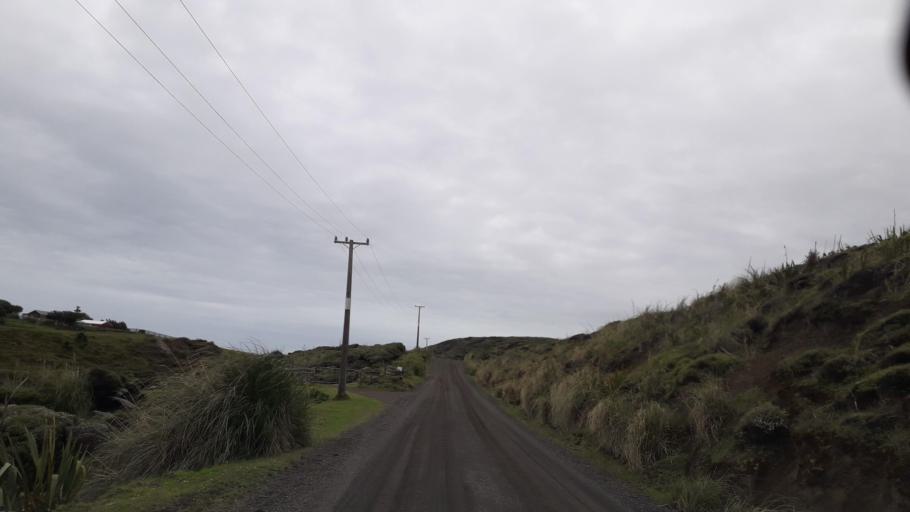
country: NZ
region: Northland
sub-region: Far North District
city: Ahipara
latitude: -35.4329
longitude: 173.2798
